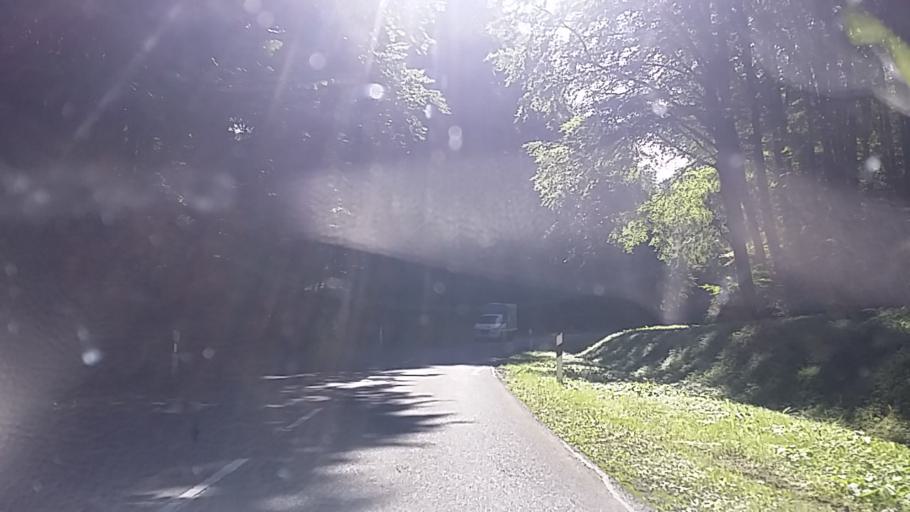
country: HU
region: Baranya
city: Pecs
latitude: 46.1290
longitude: 18.1583
